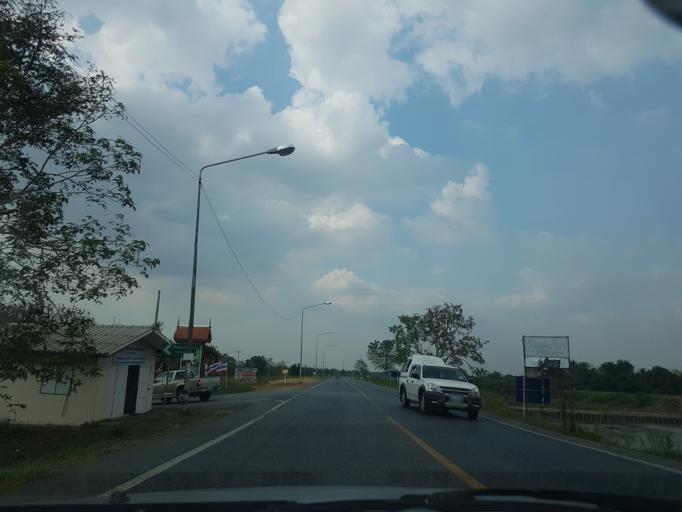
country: TH
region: Phra Nakhon Si Ayutthaya
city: Phachi
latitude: 14.4780
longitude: 100.7432
